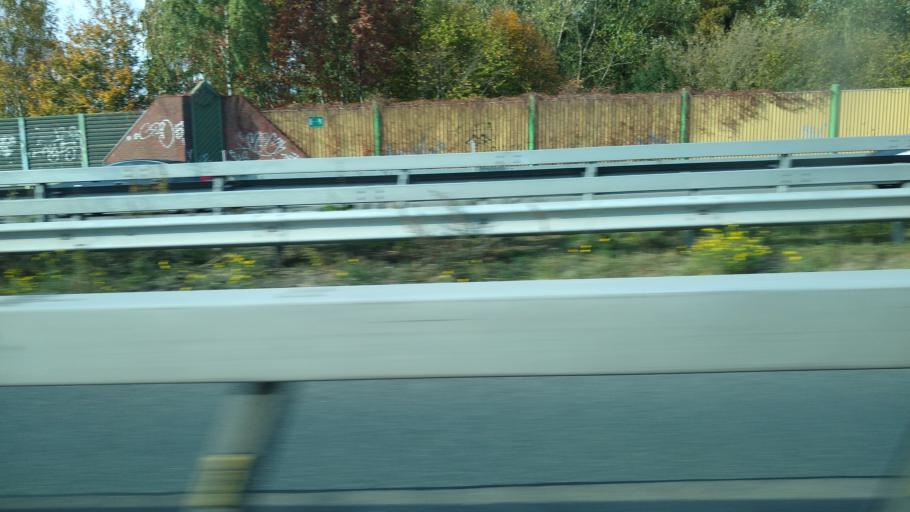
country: DE
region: Lower Saxony
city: Oldenburg
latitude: 53.1655
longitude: 8.2189
